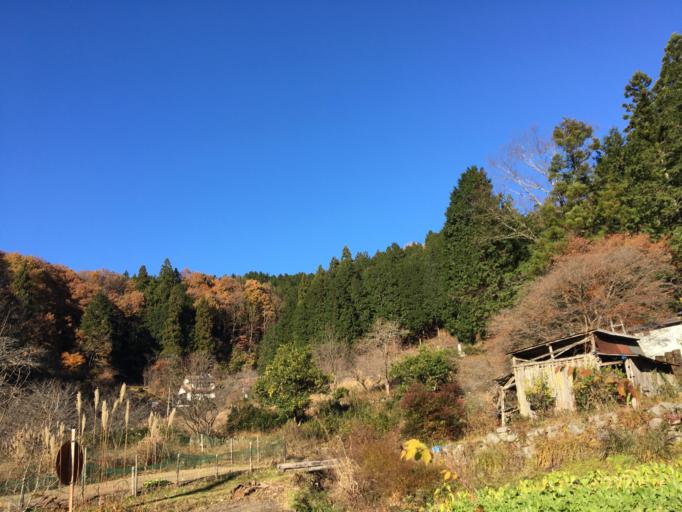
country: JP
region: Saitama
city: Ogawa
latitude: 36.0162
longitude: 139.1755
